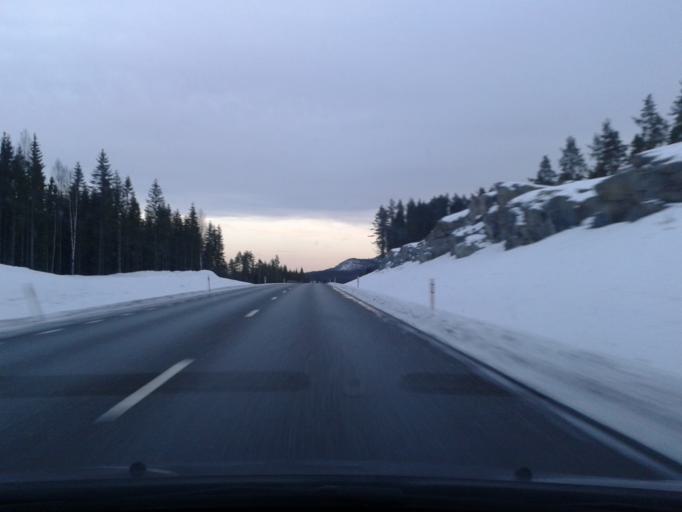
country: SE
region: Vaesternorrland
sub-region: Kramfors Kommun
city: Bollstabruk
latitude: 63.0547
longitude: 17.6142
